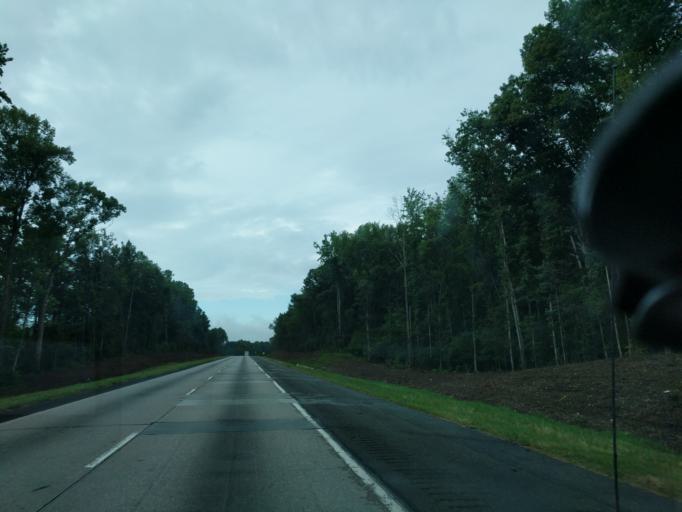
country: US
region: Georgia
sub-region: Jackson County
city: Commerce
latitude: 34.2771
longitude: -83.4333
